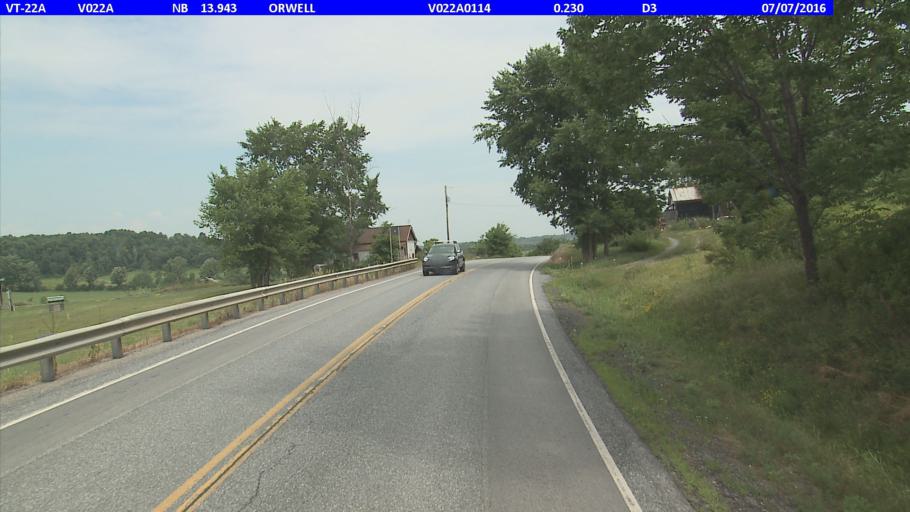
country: US
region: New York
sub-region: Essex County
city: Ticonderoga
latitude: 43.7607
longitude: -73.3125
